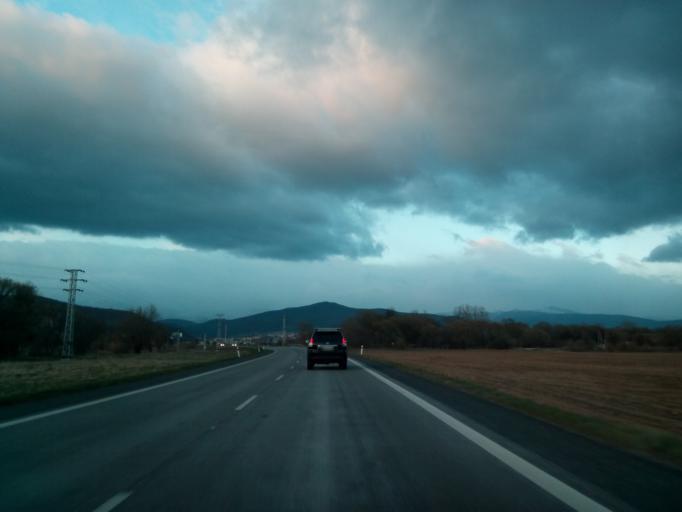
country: SK
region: Kosicky
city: Roznava
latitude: 48.6258
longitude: 20.5001
